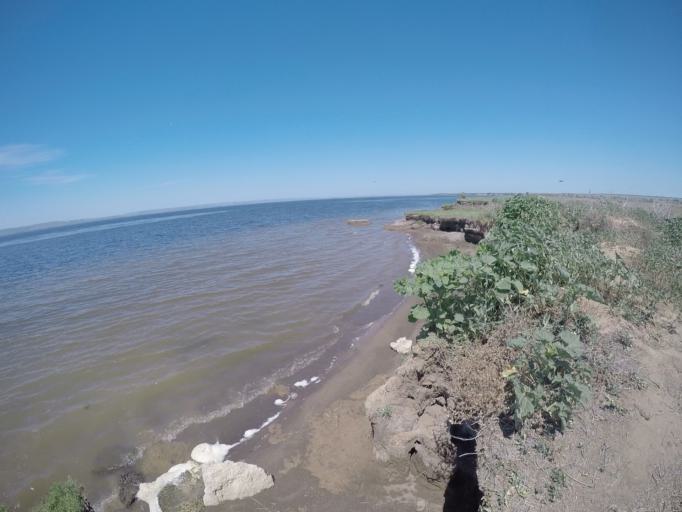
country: RU
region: Saratov
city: Krasnoarmeysk
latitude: 51.1552
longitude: 45.8970
